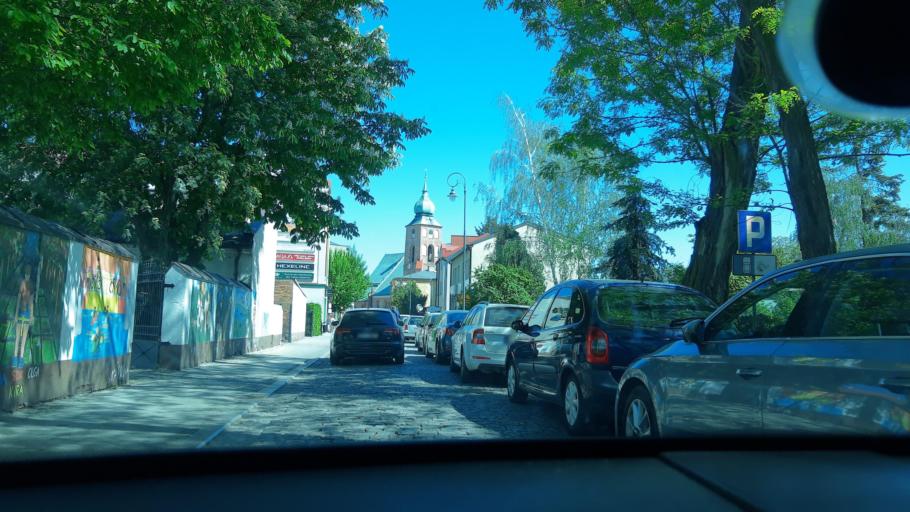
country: PL
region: Lodz Voivodeship
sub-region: Powiat sieradzki
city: Sieradz
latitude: 51.5936
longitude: 18.7360
